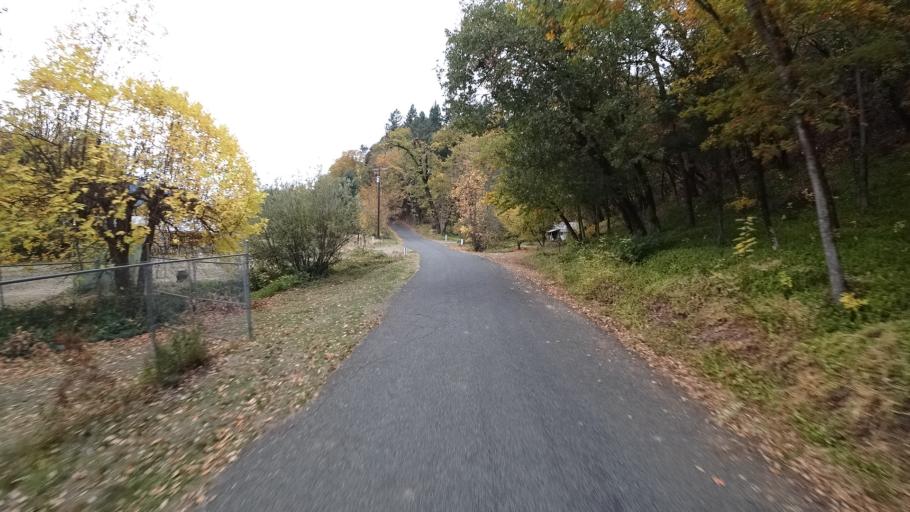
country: US
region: California
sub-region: Siskiyou County
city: Happy Camp
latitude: 41.8072
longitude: -123.3677
